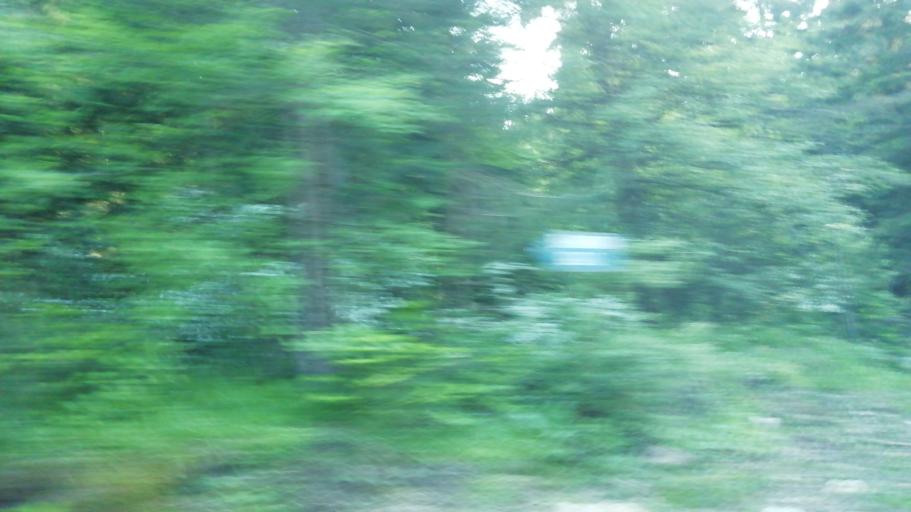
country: TR
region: Karabuk
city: Eskipazar
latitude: 41.0507
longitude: 32.5409
